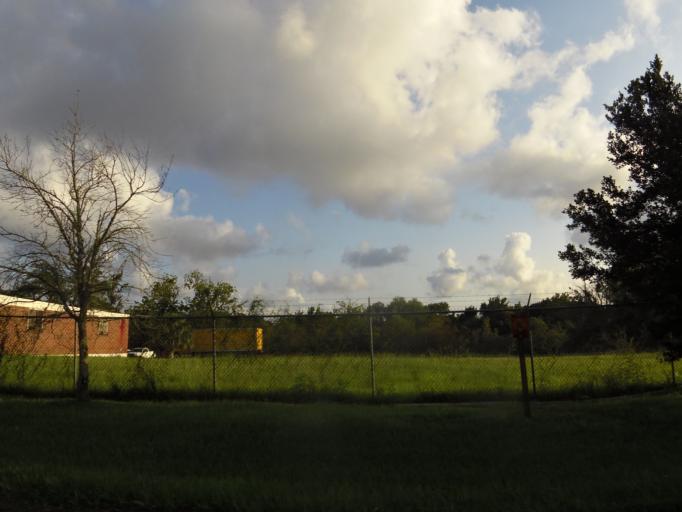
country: US
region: Florida
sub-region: Duval County
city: Jacksonville
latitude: 30.3295
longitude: -81.6877
